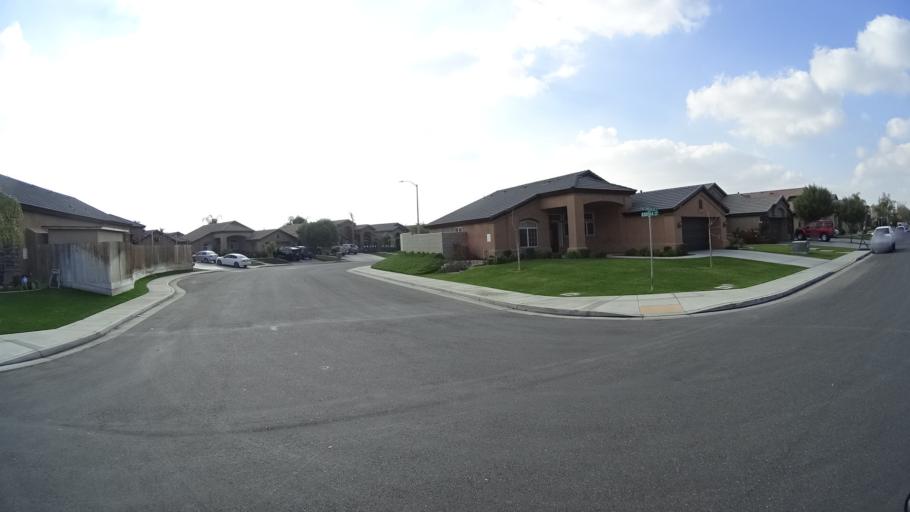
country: US
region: California
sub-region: Kern County
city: Greenacres
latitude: 35.3087
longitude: -119.1063
